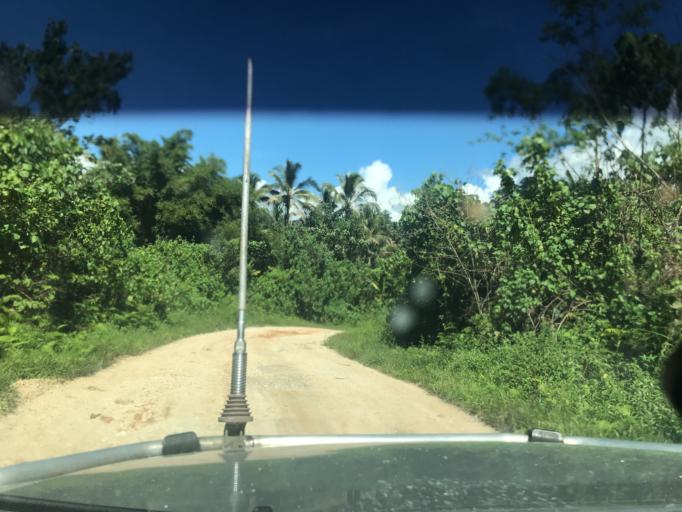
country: SB
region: Malaita
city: Auki
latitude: -8.7301
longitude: 160.9007
